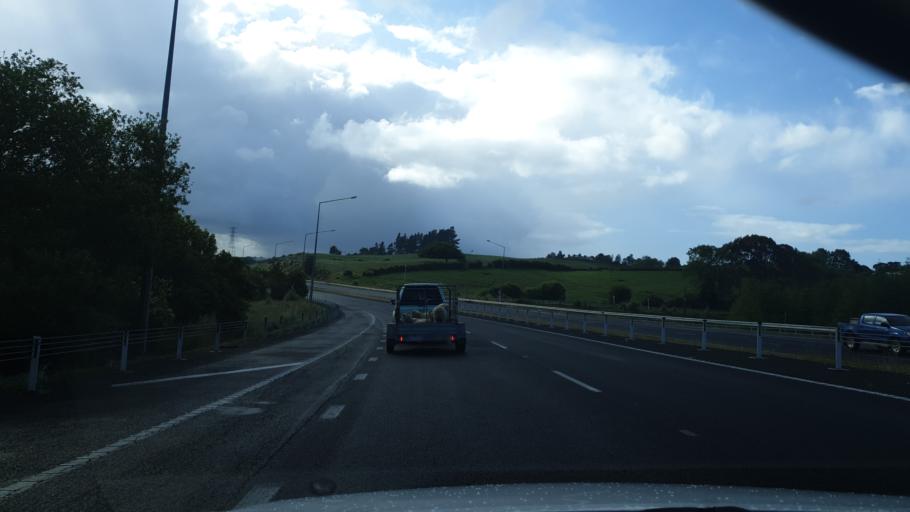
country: NZ
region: Auckland
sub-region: Auckland
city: Pukekohe East
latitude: -37.2521
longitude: 175.0308
